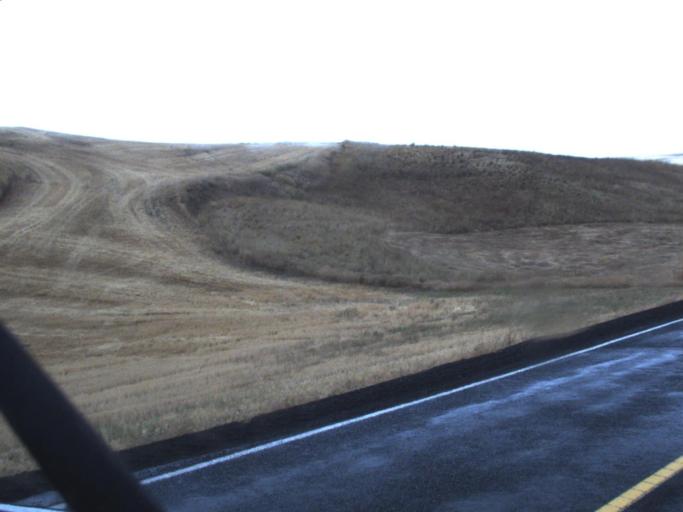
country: US
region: Washington
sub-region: Spokane County
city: Cheney
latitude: 47.1563
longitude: -117.8622
